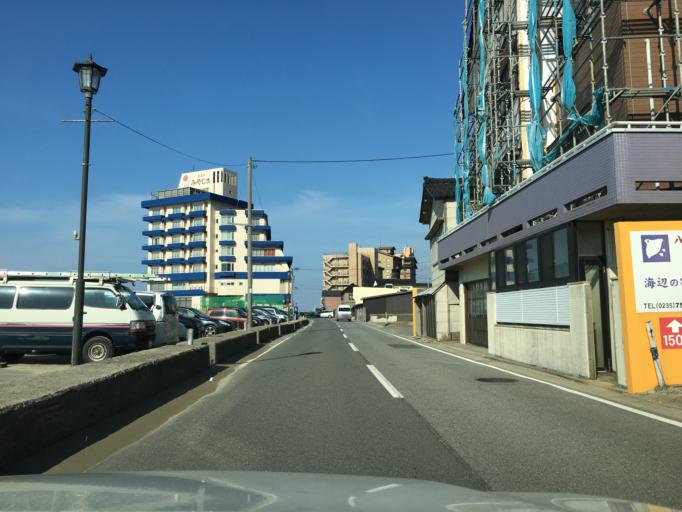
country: JP
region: Yamagata
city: Tsuruoka
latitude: 38.7767
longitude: 139.7489
